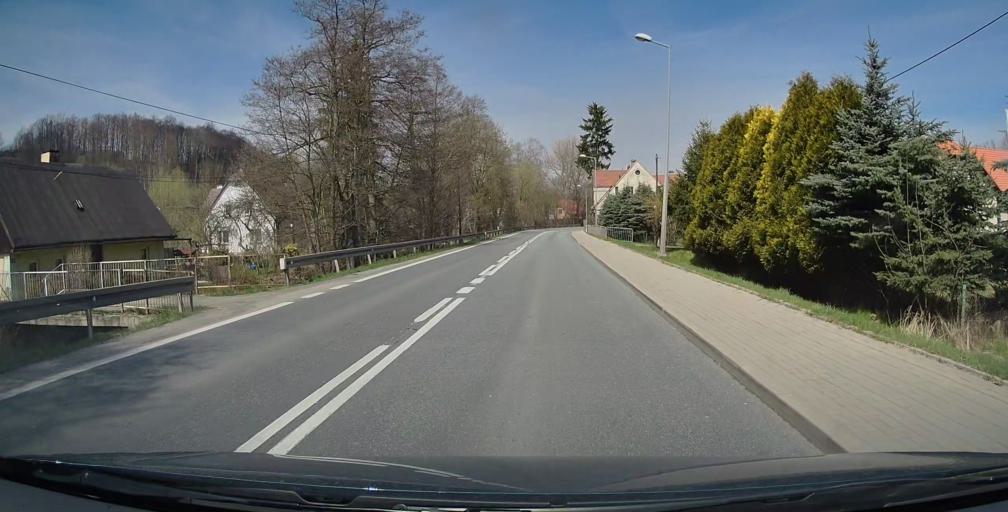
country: PL
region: Lower Silesian Voivodeship
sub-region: Powiat klodzki
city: Kudowa-Zdroj
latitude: 50.4190
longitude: 16.2613
